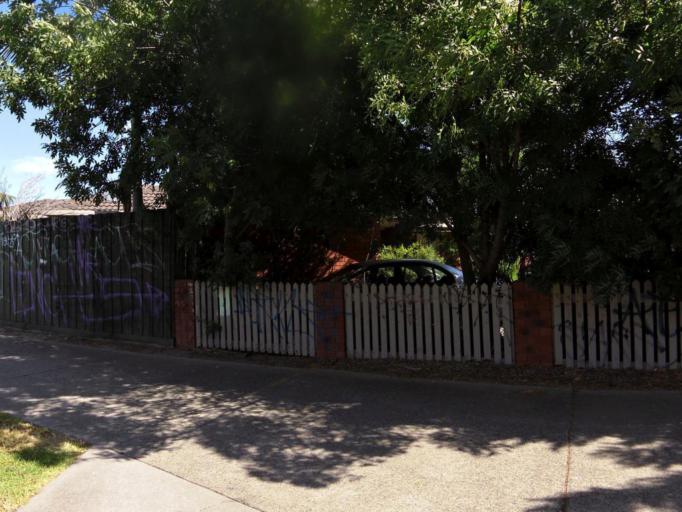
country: AU
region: Victoria
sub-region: Kingston
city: Clayton South
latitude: -37.9286
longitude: 145.1253
